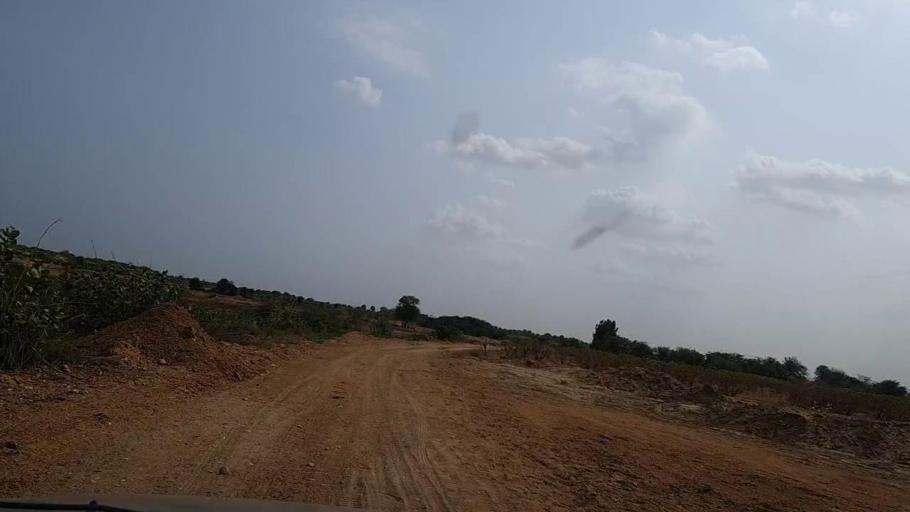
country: PK
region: Sindh
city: Kotri
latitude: 25.2669
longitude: 68.2657
